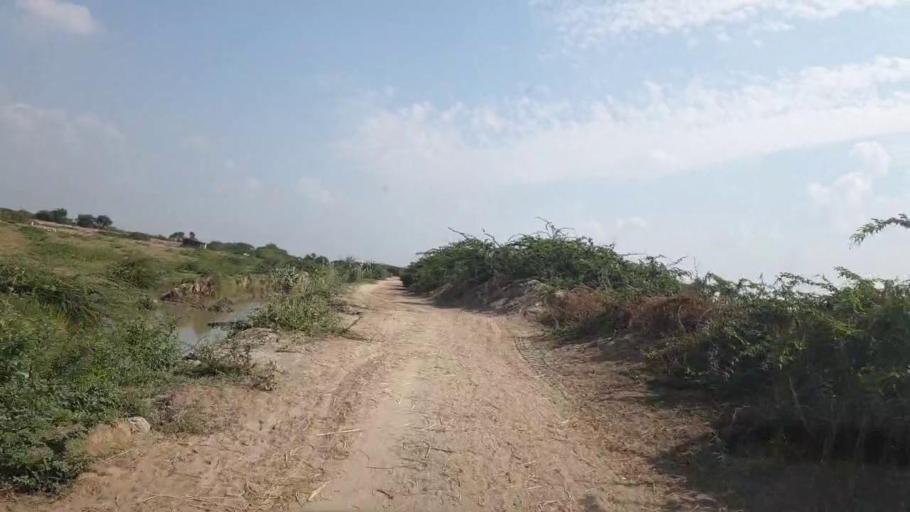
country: PK
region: Sindh
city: Badin
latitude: 24.4774
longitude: 68.6000
